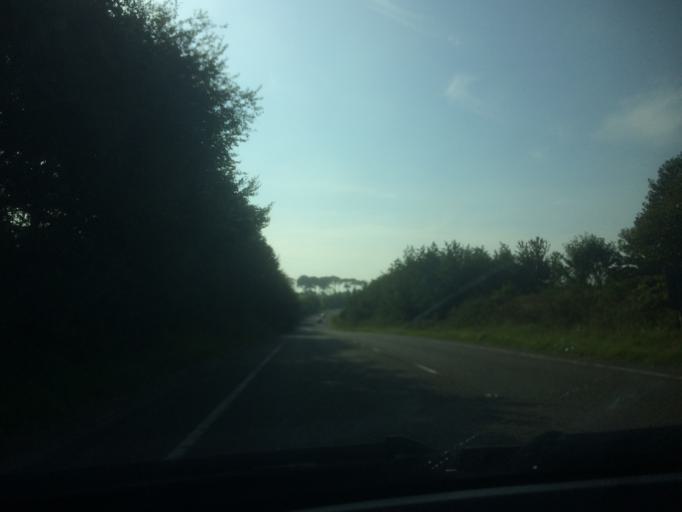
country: GB
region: England
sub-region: Cornwall
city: Pillaton
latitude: 50.4622
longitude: -4.2648
